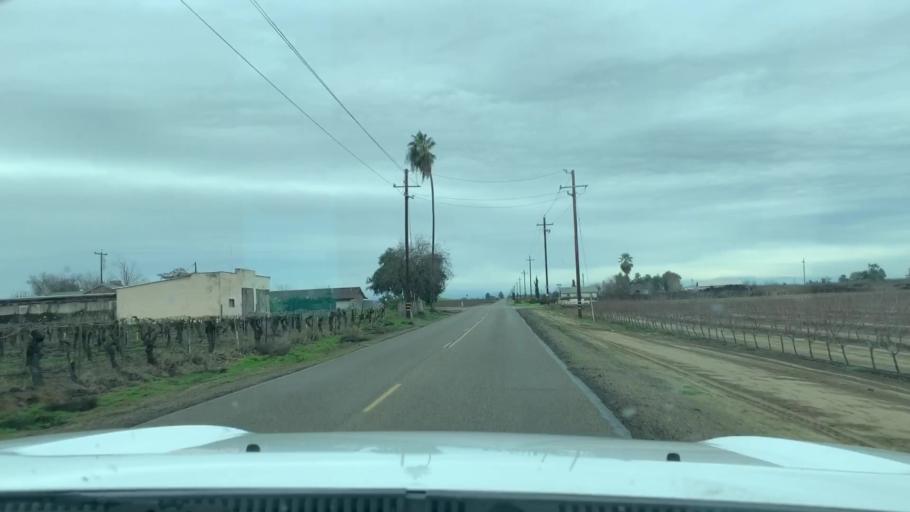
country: US
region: California
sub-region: Fresno County
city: Caruthers
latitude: 36.5474
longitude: -119.7743
